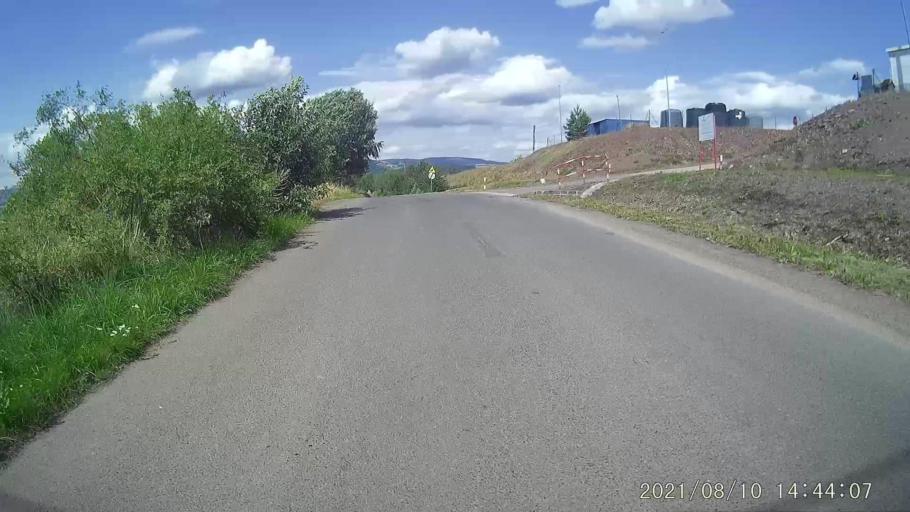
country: PL
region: Lower Silesian Voivodeship
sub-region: Powiat klodzki
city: Radkow
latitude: 50.5435
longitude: 16.4249
